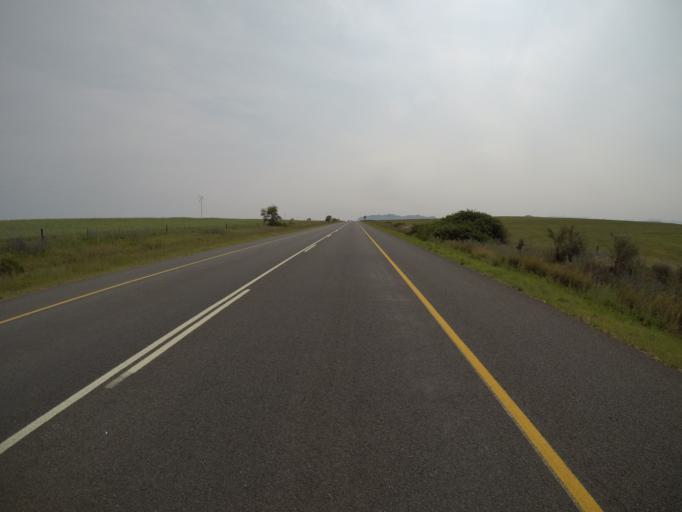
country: ZA
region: Western Cape
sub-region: West Coast District Municipality
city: Malmesbury
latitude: -33.5236
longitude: 18.8469
